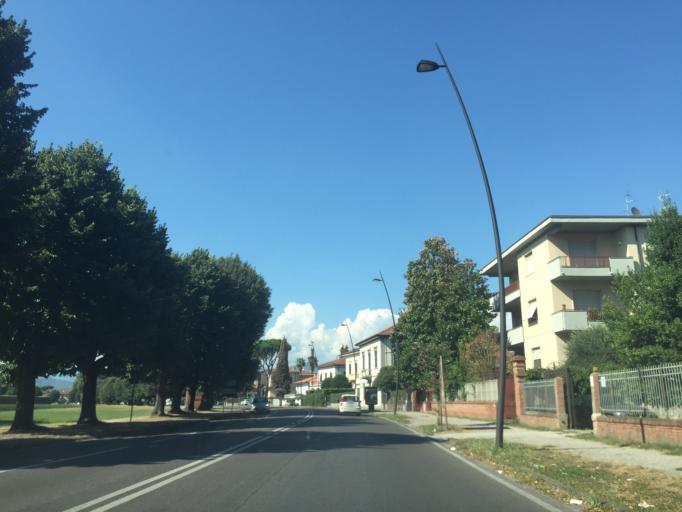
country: IT
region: Tuscany
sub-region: Provincia di Lucca
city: Lucca
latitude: 43.8442
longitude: 10.5162
